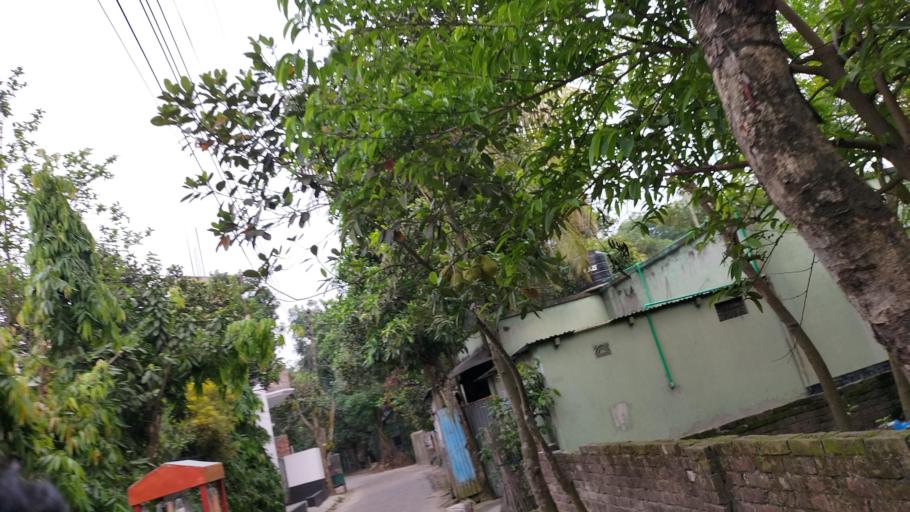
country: BD
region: Dhaka
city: Azimpur
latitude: 23.6826
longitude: 90.3147
